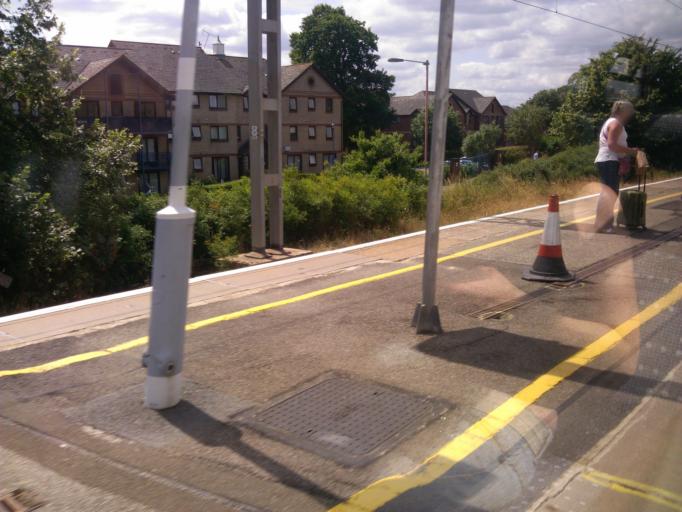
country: GB
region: England
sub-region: Essex
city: Colchester
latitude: 51.9002
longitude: 0.8950
